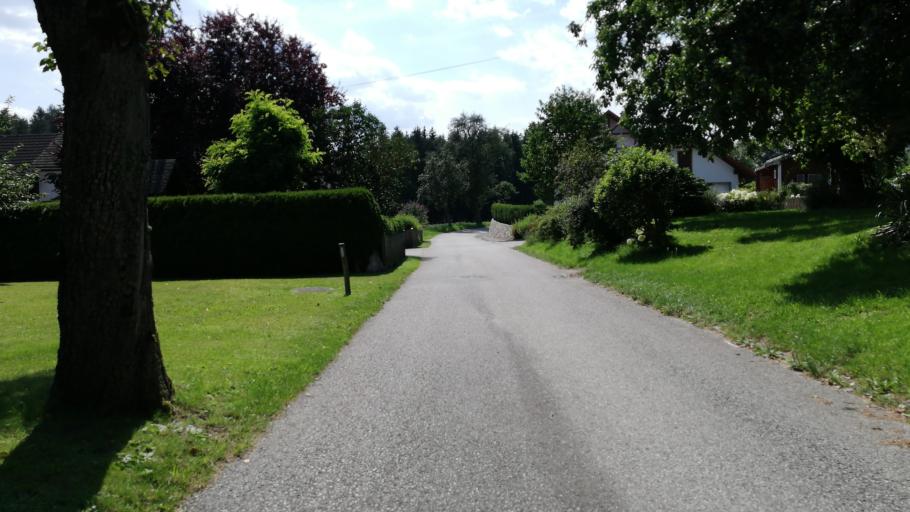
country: AT
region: Upper Austria
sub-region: Wels-Land
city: Edt bei Lambach
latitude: 48.1717
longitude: 13.9049
